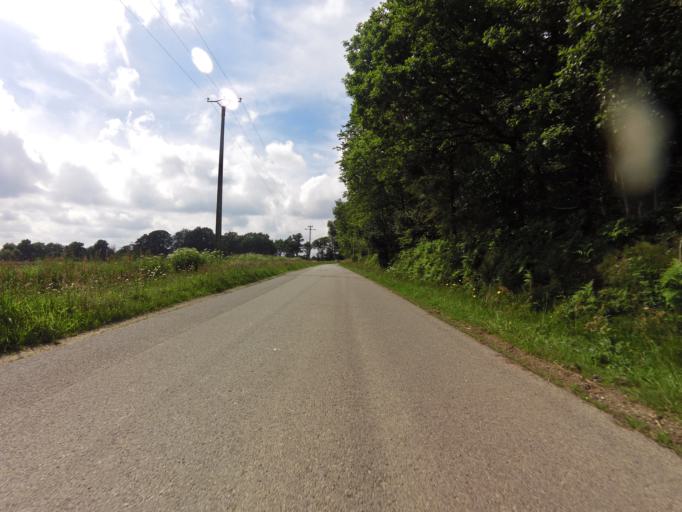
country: FR
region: Brittany
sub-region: Departement du Morbihan
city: Malansac
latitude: 47.6834
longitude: -2.3044
